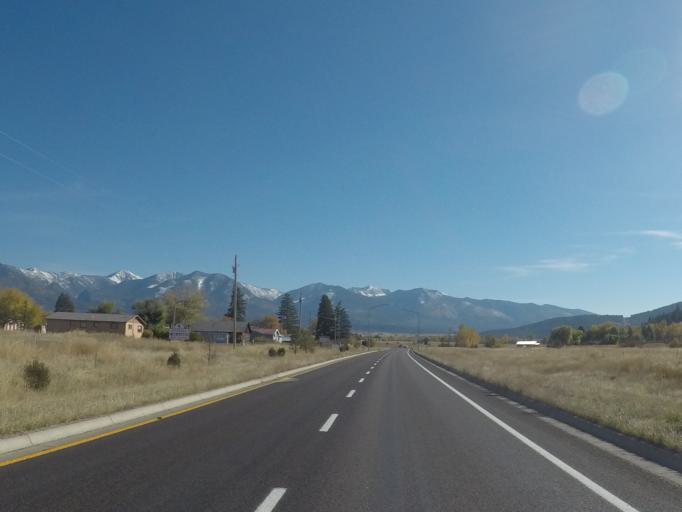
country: US
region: Montana
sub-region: Missoula County
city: Frenchtown
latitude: 47.1626
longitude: -114.0883
